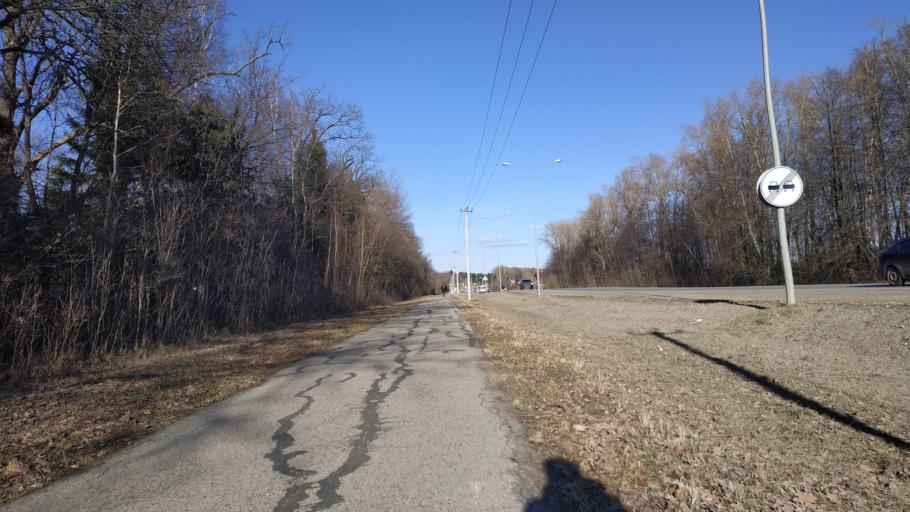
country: RU
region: Chuvashia
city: Ishley
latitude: 56.1321
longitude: 47.0769
